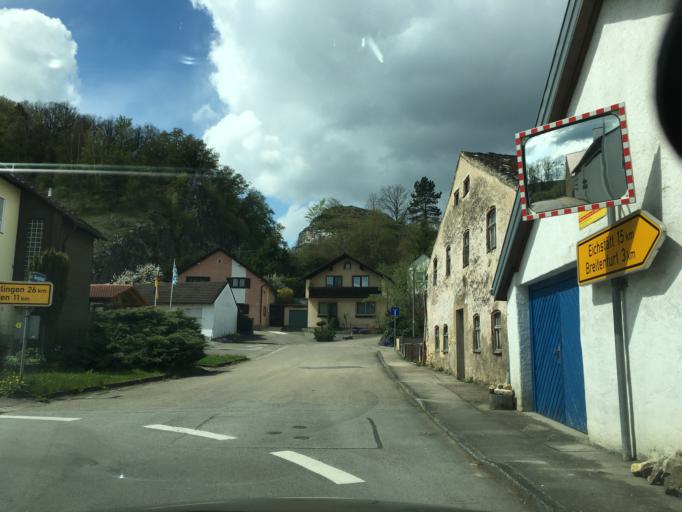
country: DE
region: Bavaria
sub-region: Upper Bavaria
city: Schernfeld
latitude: 48.8738
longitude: 11.0723
